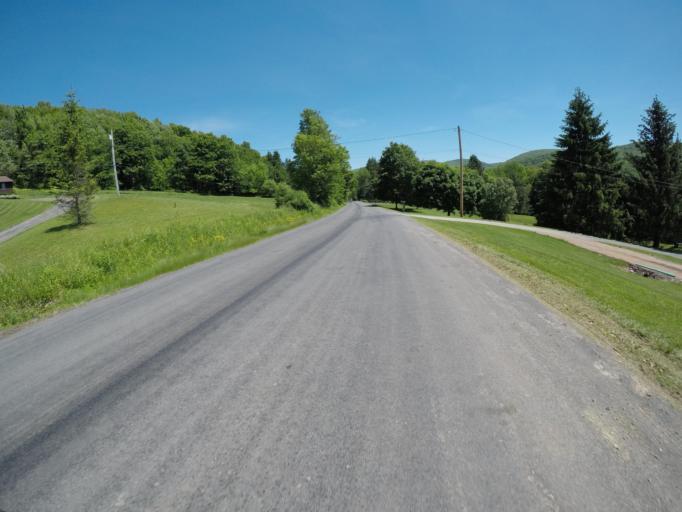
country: US
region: New York
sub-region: Delaware County
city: Delhi
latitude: 42.1848
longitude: -74.7921
